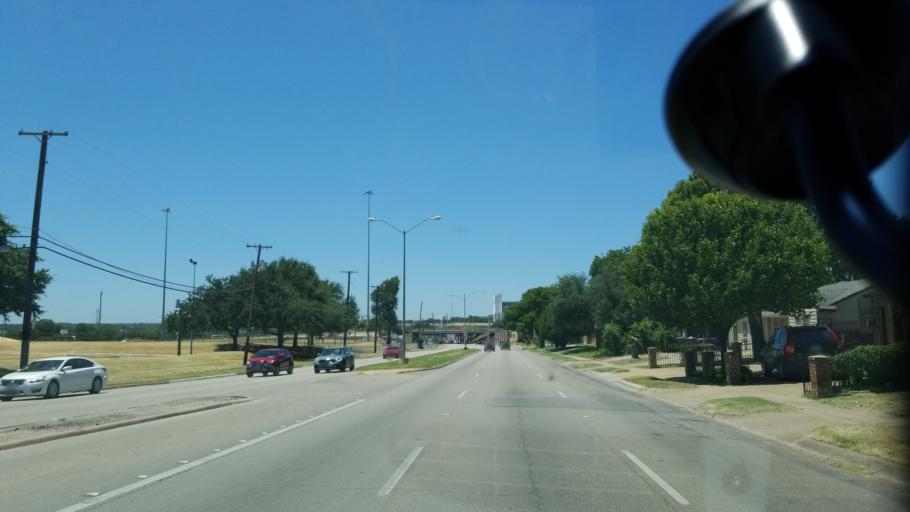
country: US
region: Texas
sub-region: Dallas County
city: Cockrell Hill
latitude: 32.7060
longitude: -96.8239
